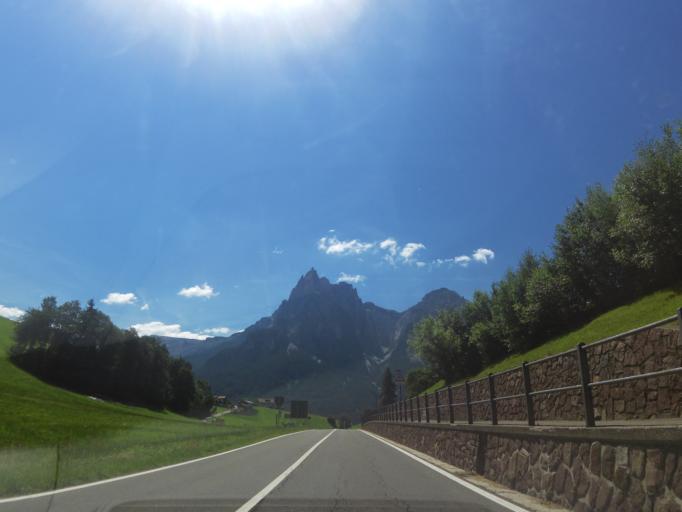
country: IT
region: Trentino-Alto Adige
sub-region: Bolzano
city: Castelrotto
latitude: 46.5563
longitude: 11.5565
